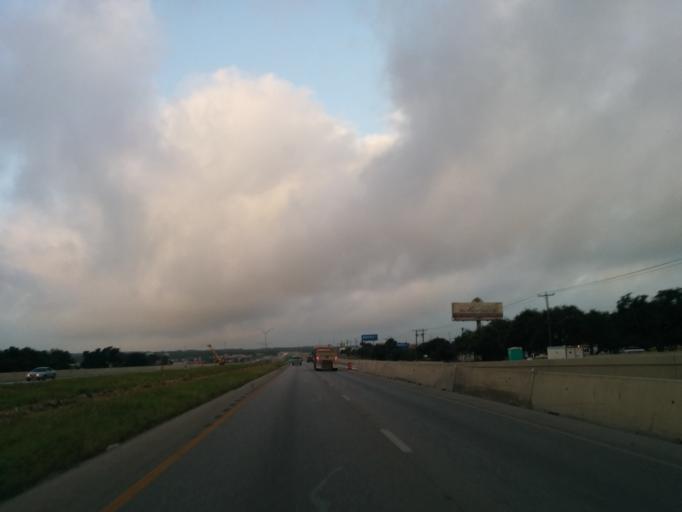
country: US
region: Texas
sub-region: Bexar County
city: Helotes
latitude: 29.5029
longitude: -98.7007
